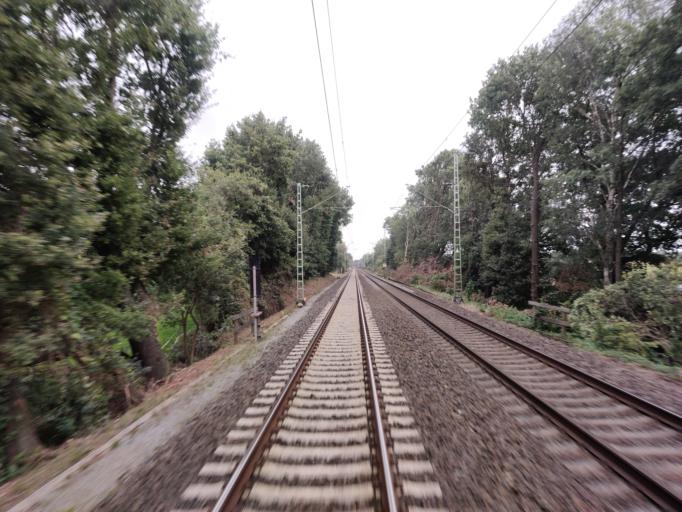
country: DE
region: Lower Saxony
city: Osterholz-Scharmbeck
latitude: 53.2000
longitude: 8.7700
